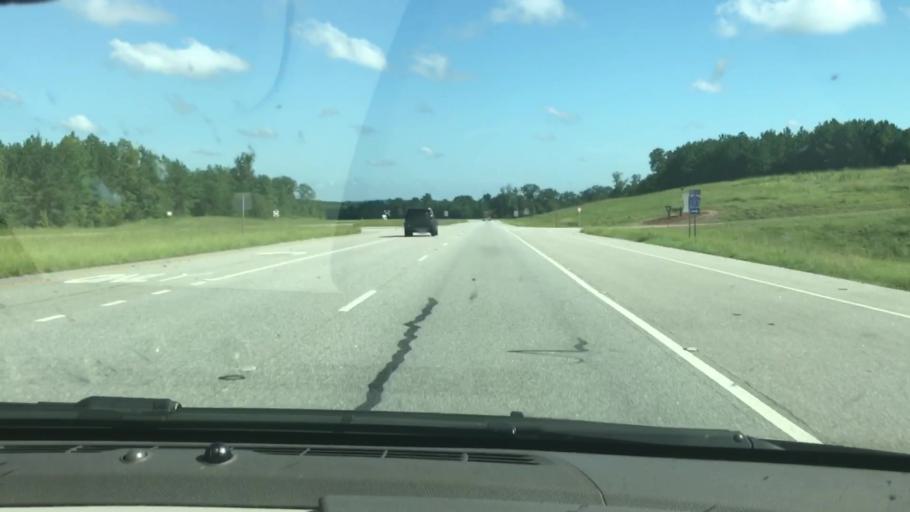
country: US
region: Alabama
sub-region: Barbour County
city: Eufaula
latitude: 32.1652
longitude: -85.1766
